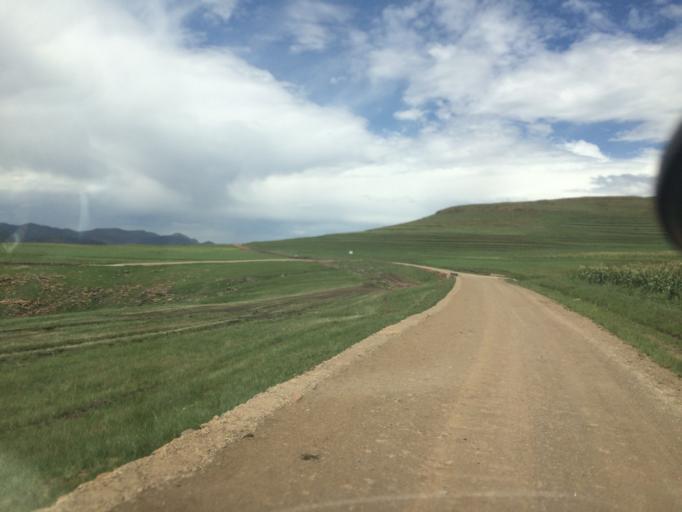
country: LS
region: Maseru
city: Nako
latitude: -29.8761
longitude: 28.0428
